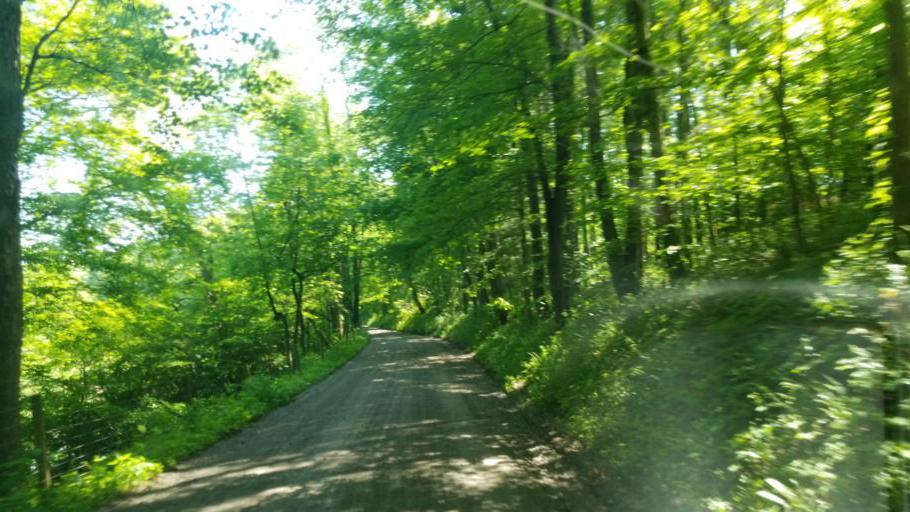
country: US
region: Ohio
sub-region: Holmes County
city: Millersburg
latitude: 40.4453
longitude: -81.8076
